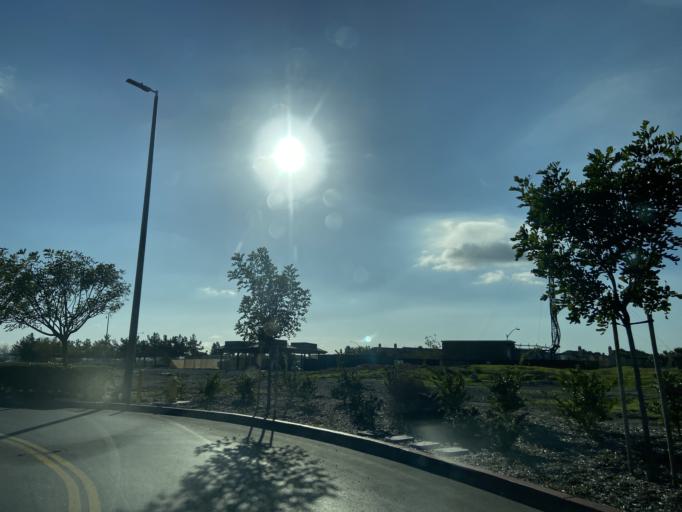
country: US
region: California
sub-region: San Diego County
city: Bonita
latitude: 32.6255
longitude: -116.9701
